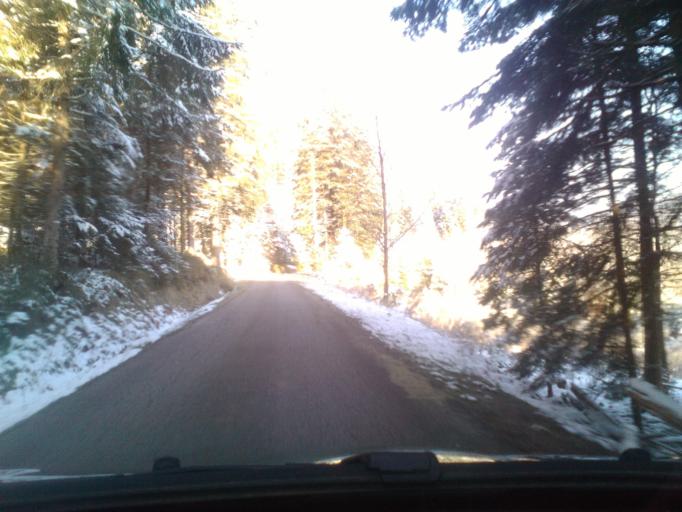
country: FR
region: Lorraine
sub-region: Departement des Vosges
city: Taintrux
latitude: 48.2360
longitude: 6.8572
